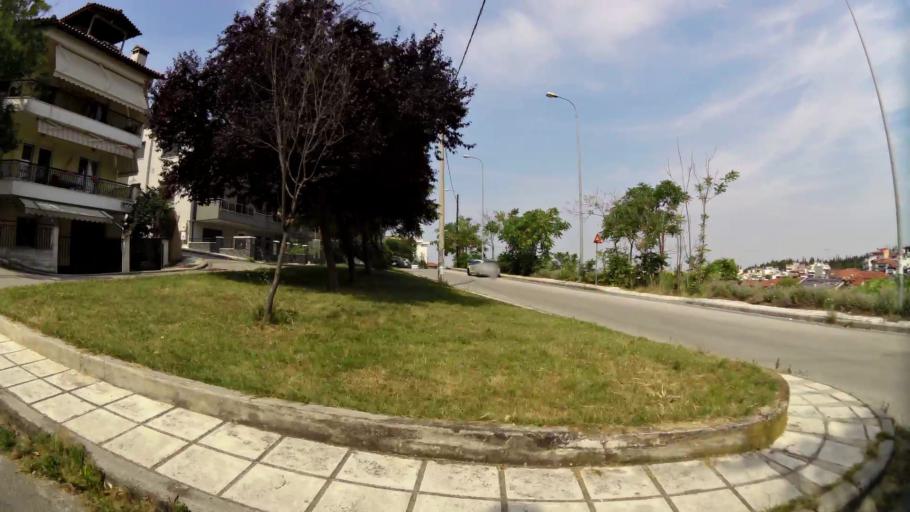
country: GR
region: Central Macedonia
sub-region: Nomos Thessalonikis
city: Agios Pavlos
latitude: 40.6453
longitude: 22.9585
